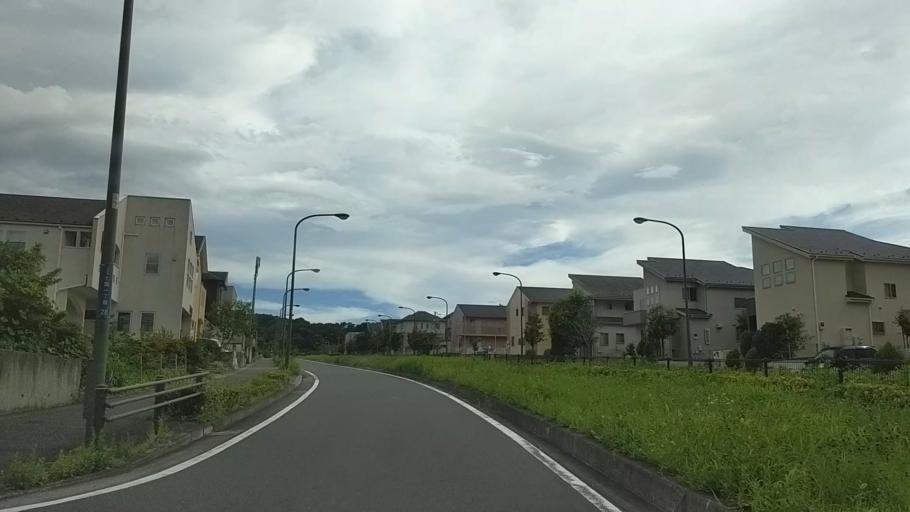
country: JP
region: Tokyo
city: Hachioji
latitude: 35.6216
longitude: 139.3274
